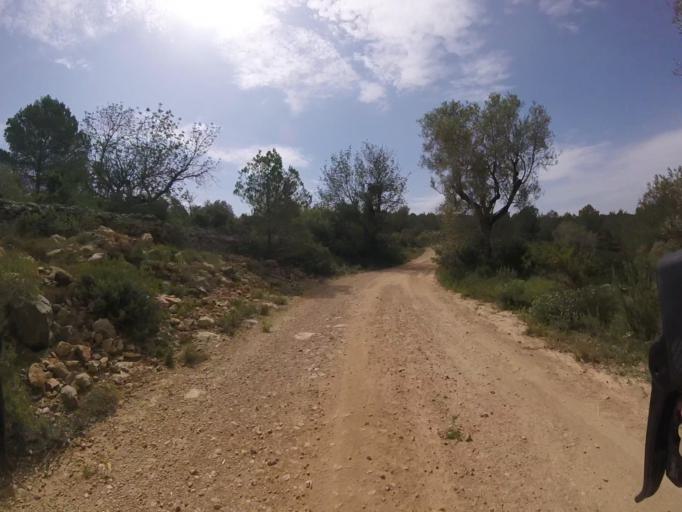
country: ES
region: Valencia
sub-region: Provincia de Castello
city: Cuevas de Vinroma
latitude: 40.2813
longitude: 0.1237
